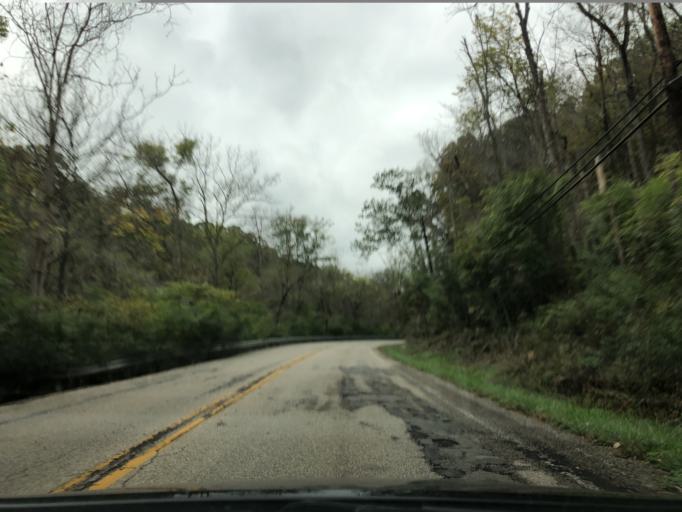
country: US
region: Ohio
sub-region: Hamilton County
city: Madeira
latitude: 39.1767
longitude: -84.3755
